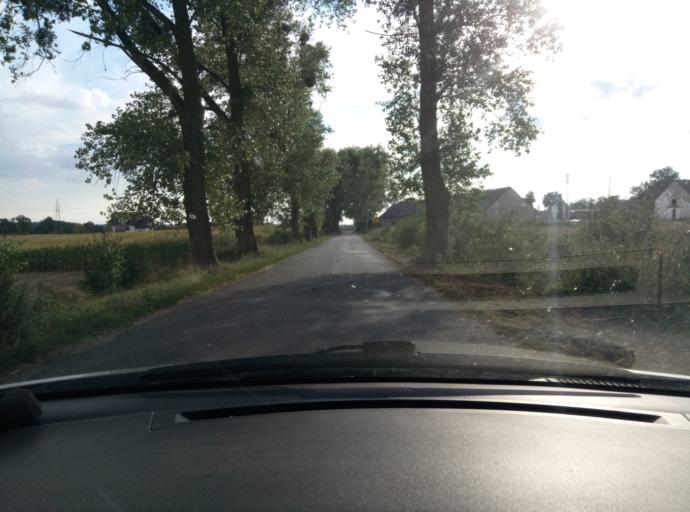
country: PL
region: Kujawsko-Pomorskie
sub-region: Powiat brodnicki
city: Jablonowo Pomorskie
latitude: 53.3863
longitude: 19.1759
